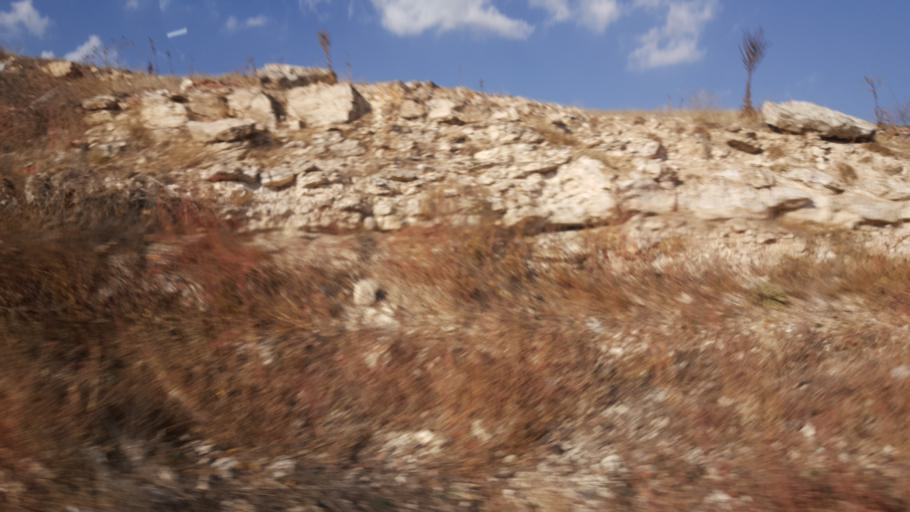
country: TR
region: Eskisehir
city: Kirka
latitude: 39.3247
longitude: 30.5644
